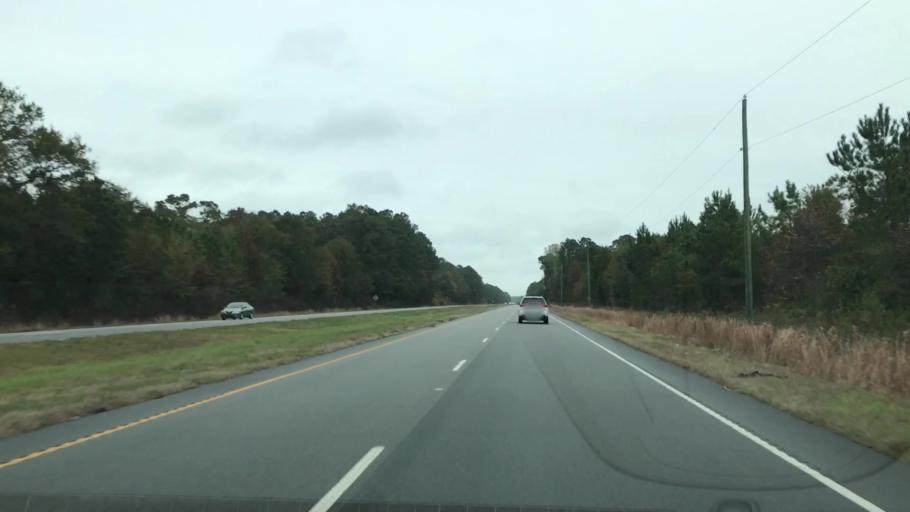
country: US
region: South Carolina
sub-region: Charleston County
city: Awendaw
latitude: 33.1050
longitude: -79.4644
